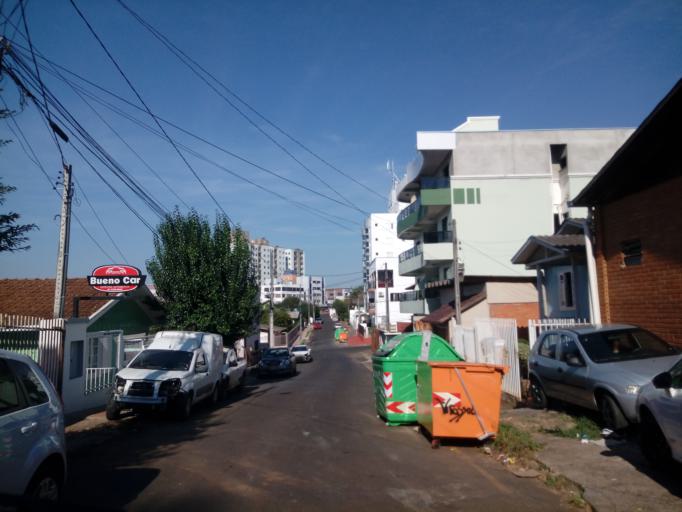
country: BR
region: Santa Catarina
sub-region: Chapeco
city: Chapeco
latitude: -27.0942
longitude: -52.6279
